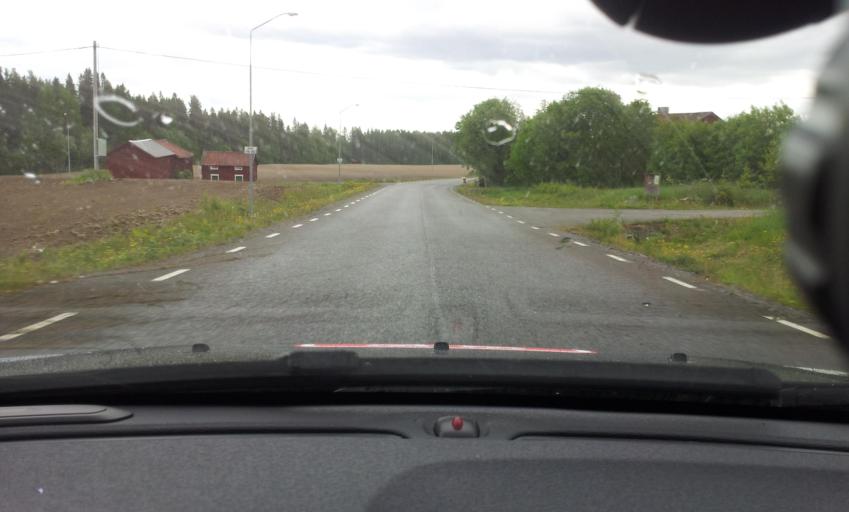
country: SE
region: Jaemtland
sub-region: OEstersunds Kommun
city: Brunflo
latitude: 63.1810
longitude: 14.9187
